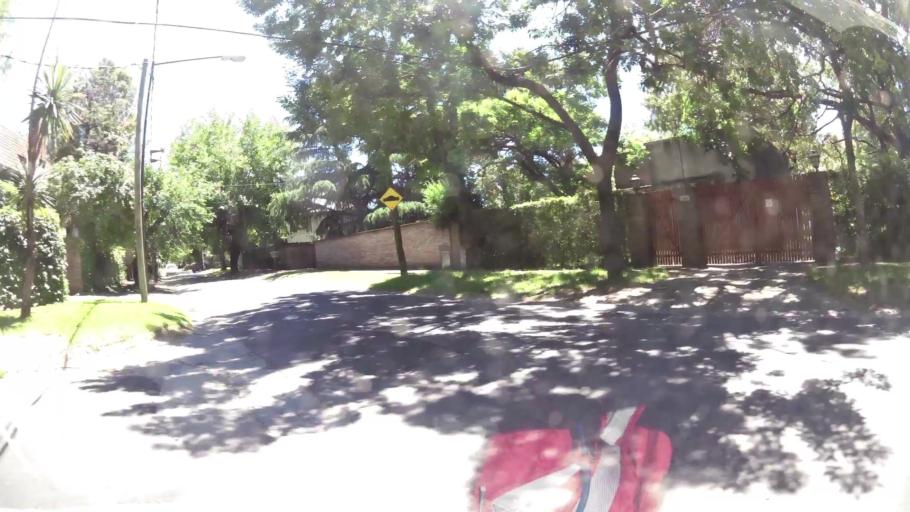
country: AR
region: Buenos Aires
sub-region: Partido de San Isidro
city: San Isidro
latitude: -34.4985
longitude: -58.5613
